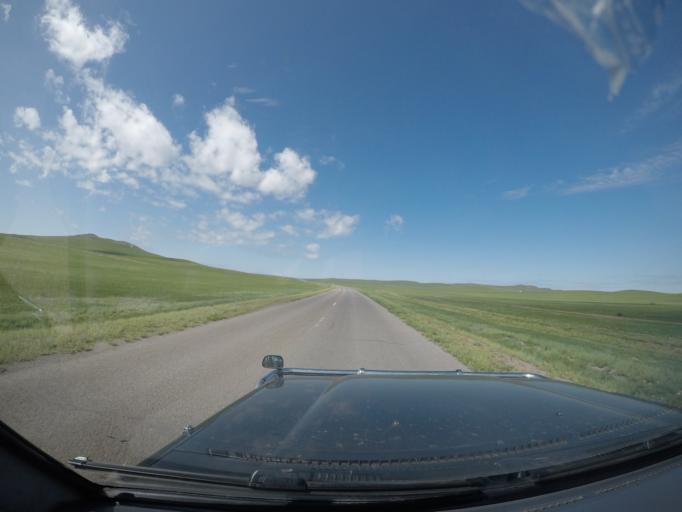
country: MN
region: Suhbaatar
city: Hanhohiy
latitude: 47.3846
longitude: 111.8635
